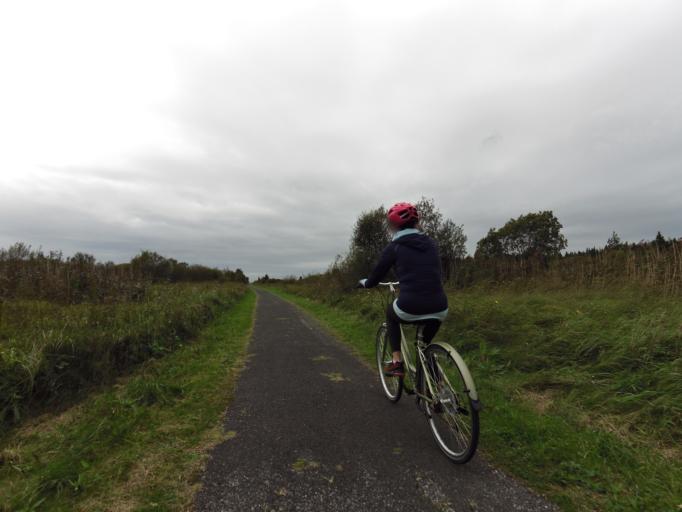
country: IE
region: Leinster
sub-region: Uibh Fhaili
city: Ferbane
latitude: 53.2138
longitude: -7.7603
